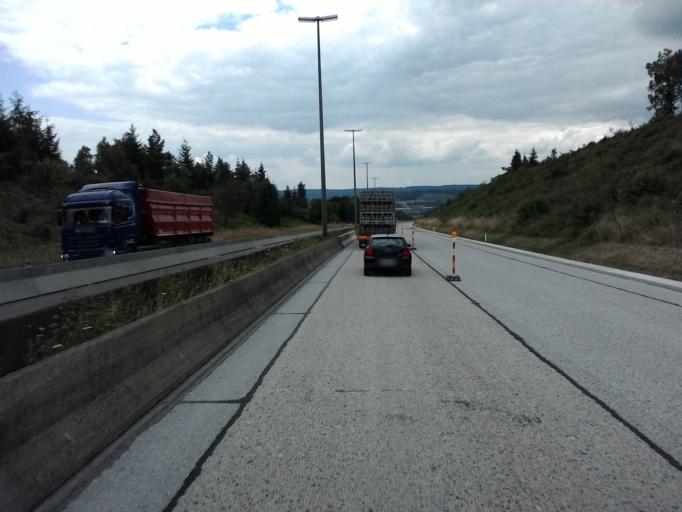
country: BE
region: Wallonia
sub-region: Province du Luxembourg
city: Manhay
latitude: 50.3298
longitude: 5.7016
